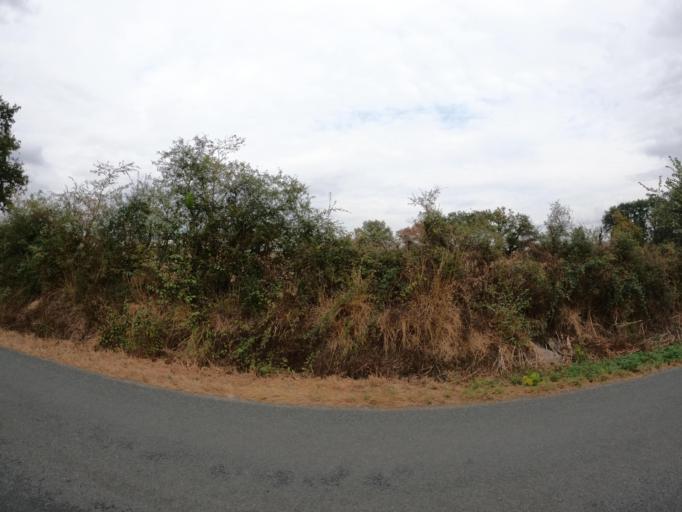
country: FR
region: Pays de la Loire
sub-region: Departement de la Vendee
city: Les Landes-Genusson
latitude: 46.9748
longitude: -1.1122
